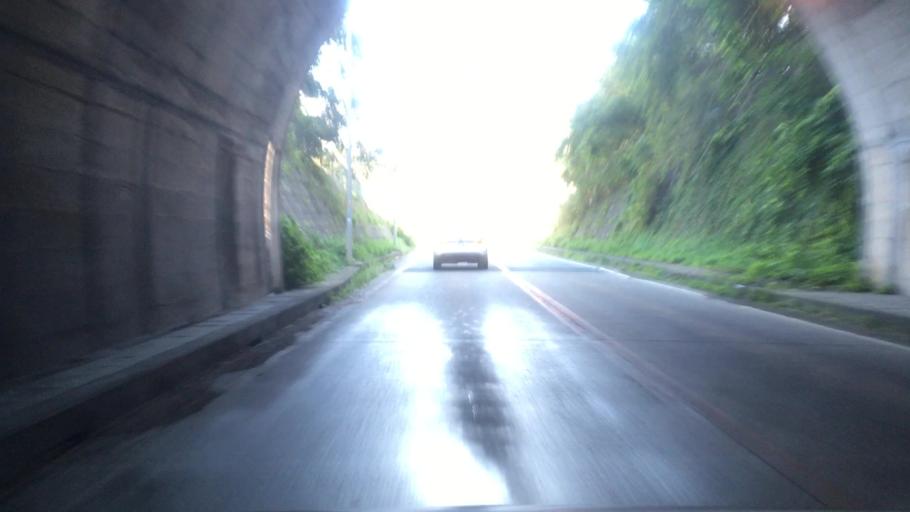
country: JP
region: Hyogo
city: Toyooka
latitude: 35.5562
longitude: 134.8321
